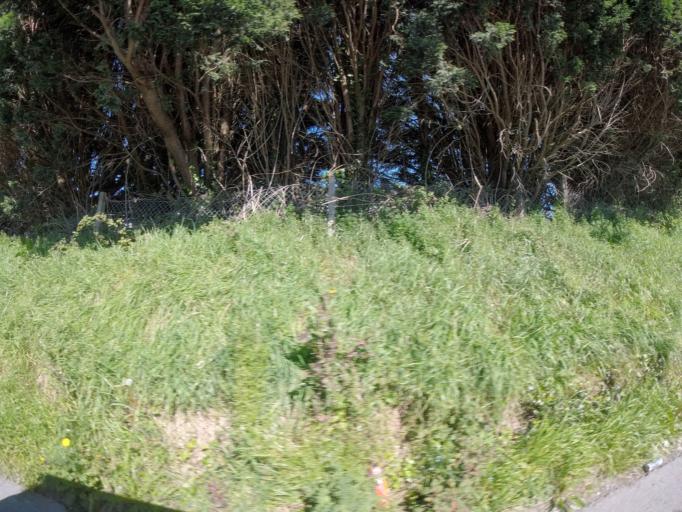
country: IE
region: Munster
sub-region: Waterford
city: Waterford
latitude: 52.2540
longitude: -7.1450
